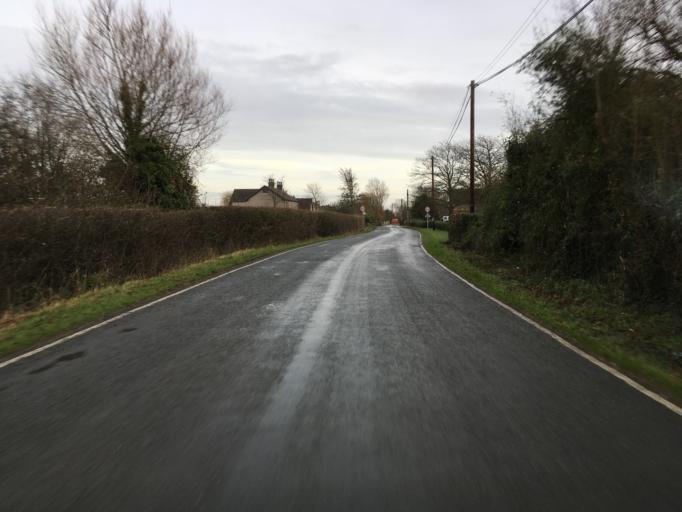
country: GB
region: Wales
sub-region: Newport
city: Goldcliff
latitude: 51.5425
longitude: -2.9236
